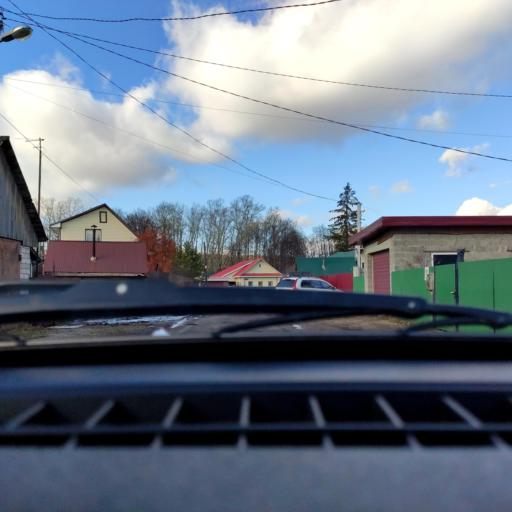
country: RU
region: Bashkortostan
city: Ufa
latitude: 54.8177
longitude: 56.1637
